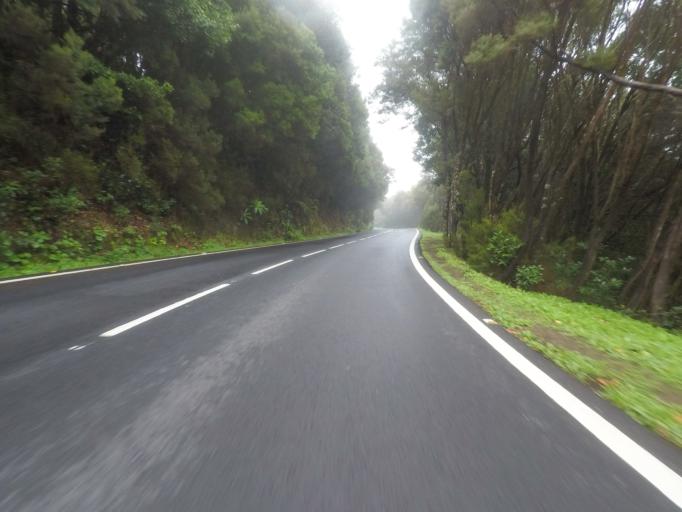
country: ES
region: Canary Islands
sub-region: Provincia de Santa Cruz de Tenerife
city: Alajero
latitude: 28.1158
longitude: -17.2437
